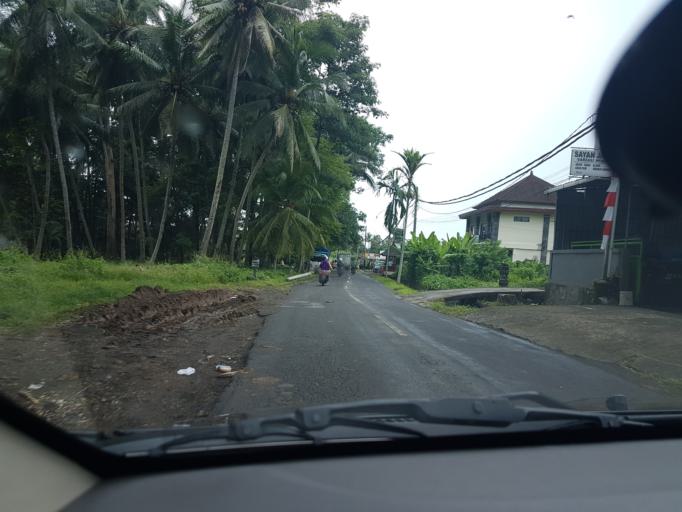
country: ID
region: Bali
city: Banjar Pande
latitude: -8.5201
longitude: 115.2394
